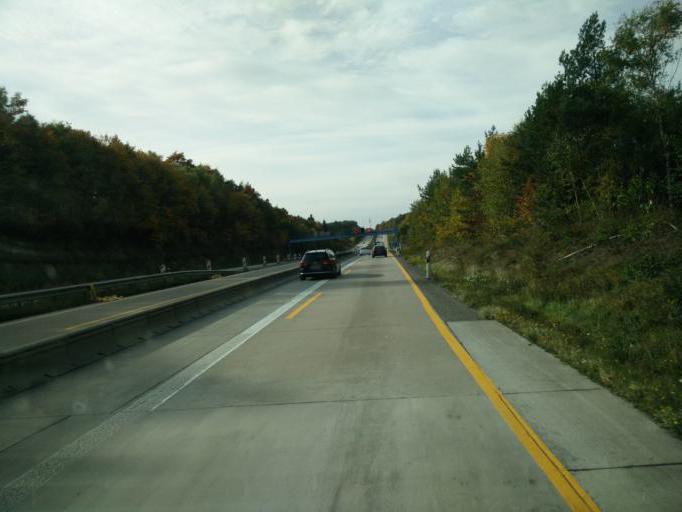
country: DE
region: Rheinland-Pfalz
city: Neuhemsbach
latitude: 49.4911
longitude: 7.9692
